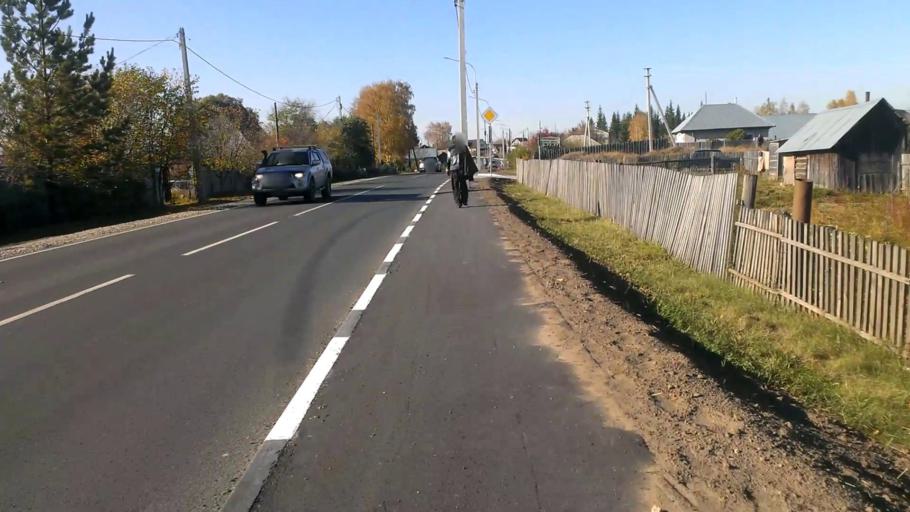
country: RU
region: Altai Krai
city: Sannikovo
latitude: 53.3143
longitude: 83.9612
